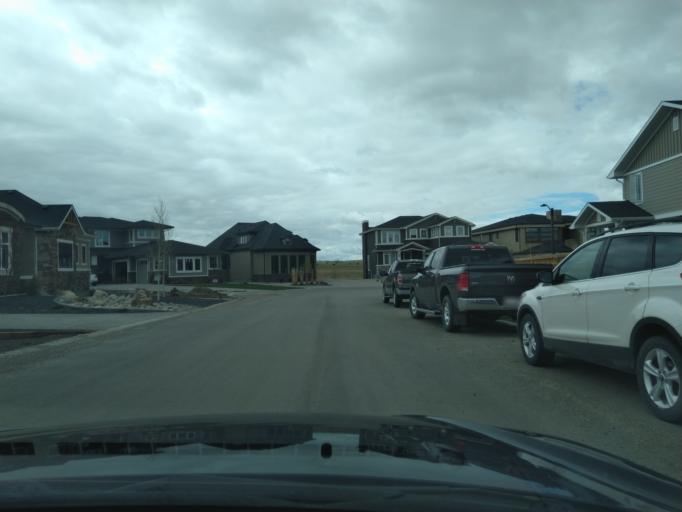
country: CA
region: Alberta
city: Cochrane
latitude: 51.1086
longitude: -114.3950
